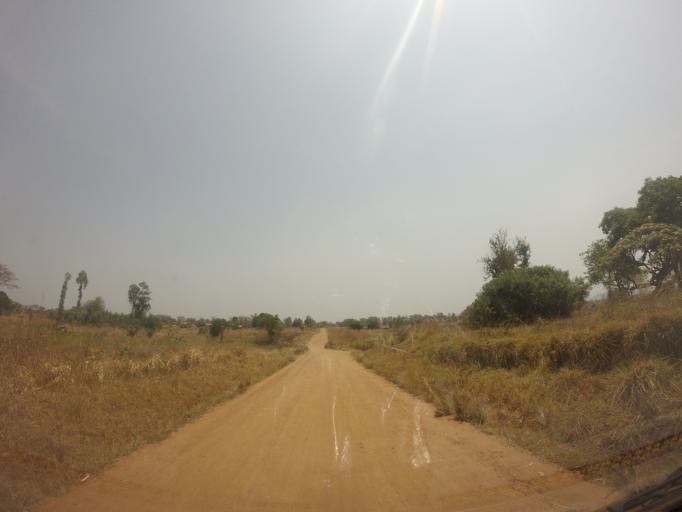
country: UG
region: Northern Region
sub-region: Arua District
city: Arua
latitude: 2.9147
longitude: 31.0188
